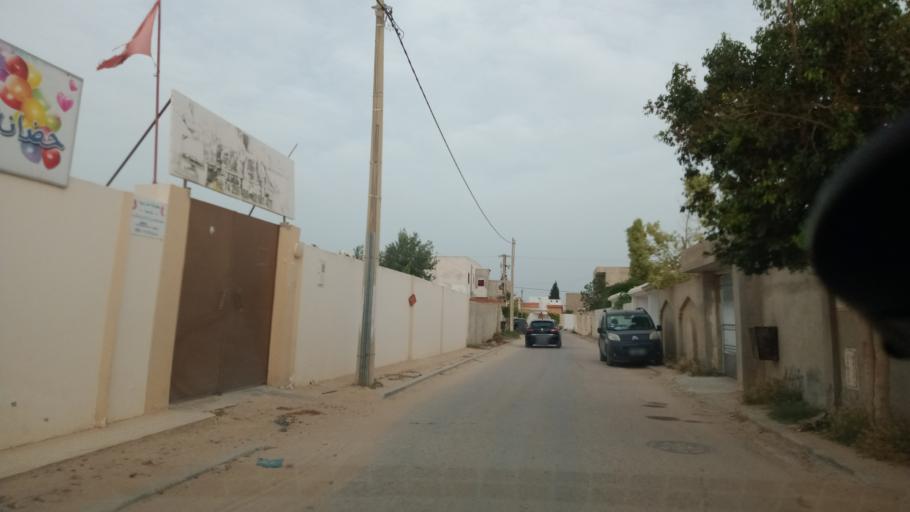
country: TN
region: Safaqis
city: Al Qarmadah
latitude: 34.7912
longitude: 10.7701
